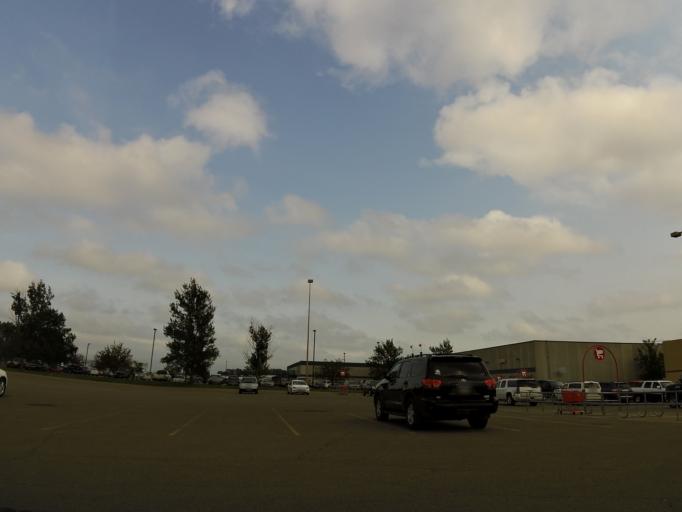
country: US
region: South Dakota
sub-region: Codington County
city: Watertown
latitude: 44.8891
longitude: -97.0838
